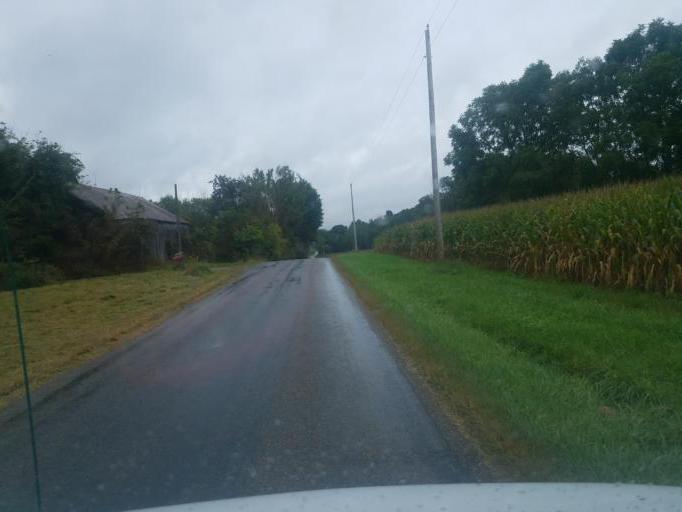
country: US
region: Ohio
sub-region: Wayne County
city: West Salem
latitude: 40.9561
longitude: -82.1190
